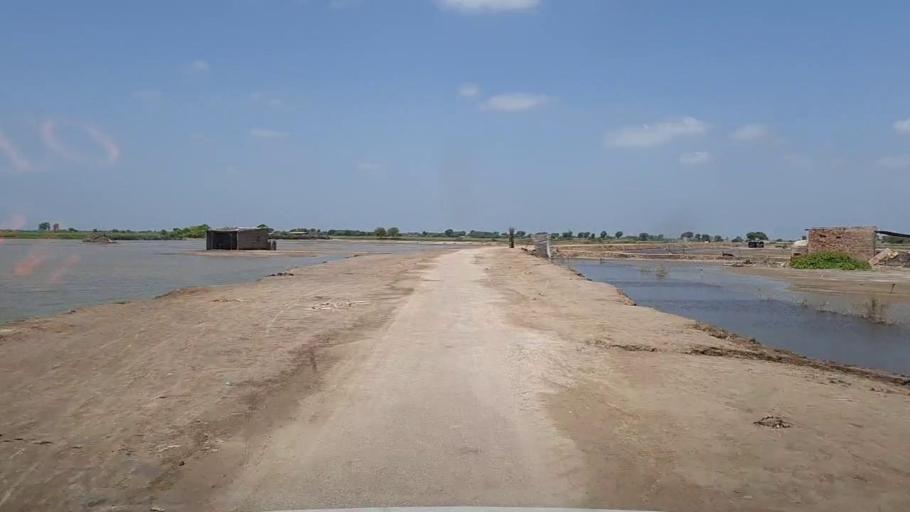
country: PK
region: Sindh
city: Kario
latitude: 24.6958
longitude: 68.5865
